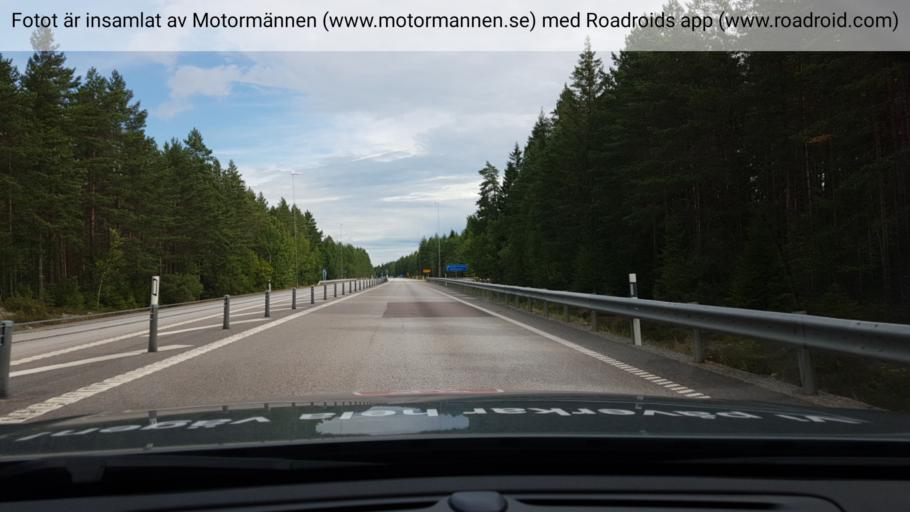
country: SE
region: Uppsala
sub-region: Heby Kommun
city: Tarnsjo
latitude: 60.2333
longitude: 16.9543
